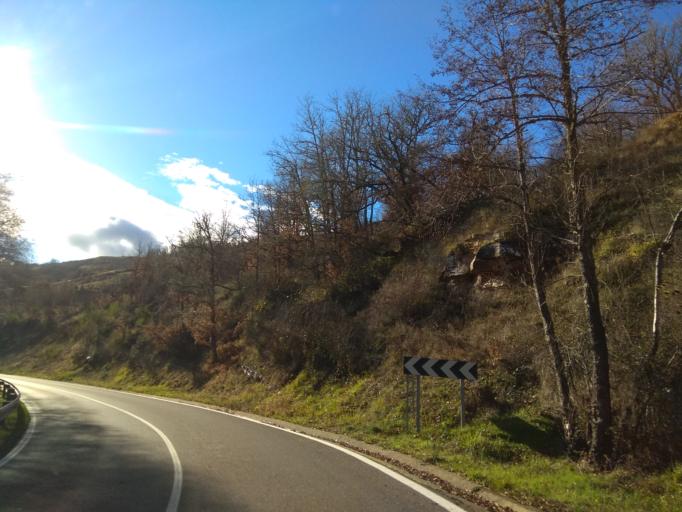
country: ES
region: Cantabria
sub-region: Provincia de Cantabria
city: San Martin de Elines
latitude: 42.8899
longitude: -3.9095
